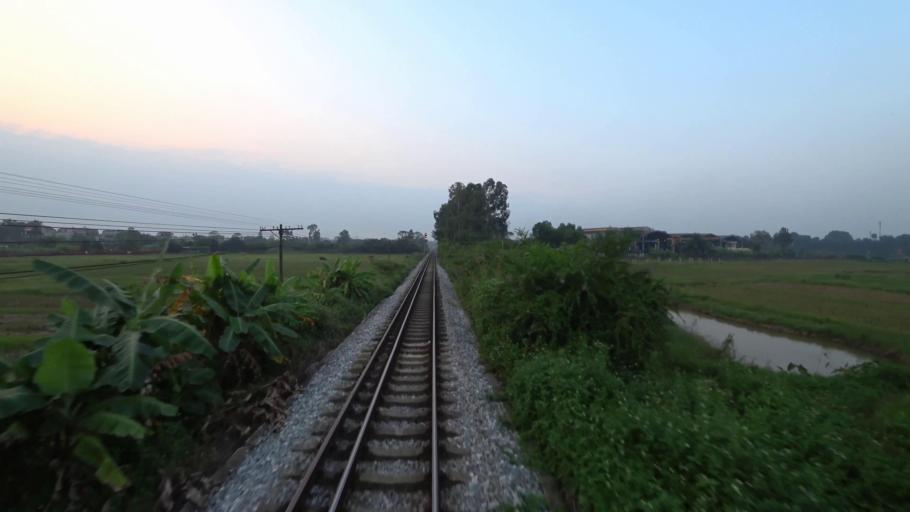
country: VN
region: Ha Noi
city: Dong Anh
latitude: 21.1498
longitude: 105.8565
